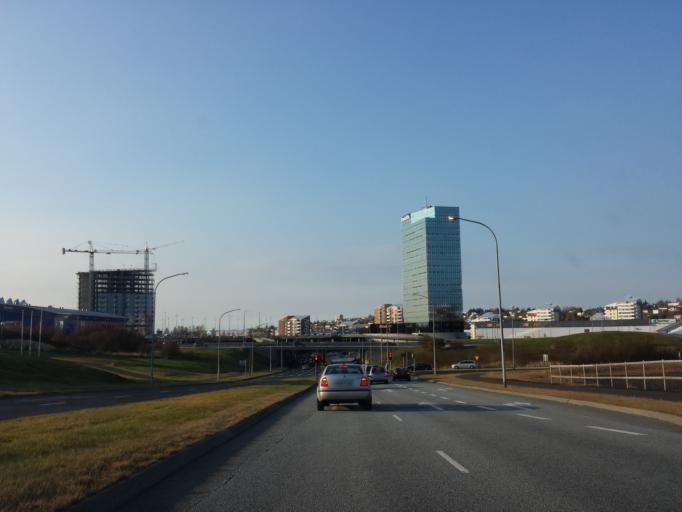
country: IS
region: Capital Region
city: Kopavogur
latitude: 64.1001
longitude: -21.8747
